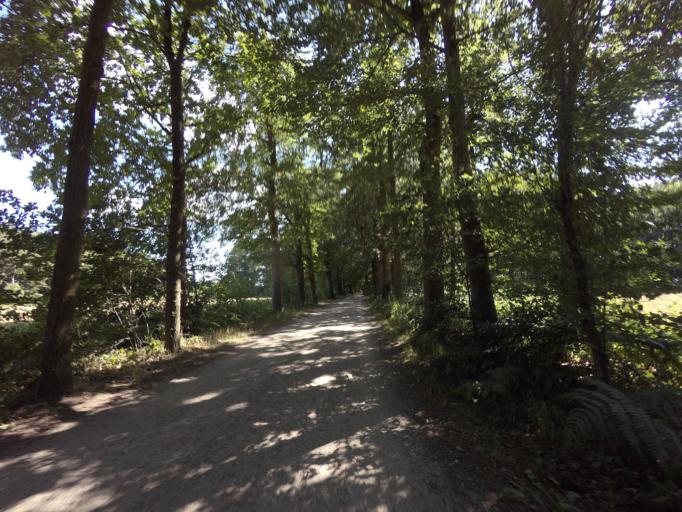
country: NL
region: Utrecht
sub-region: Gemeente De Bilt
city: De Bilt
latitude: 52.1331
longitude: 5.1712
